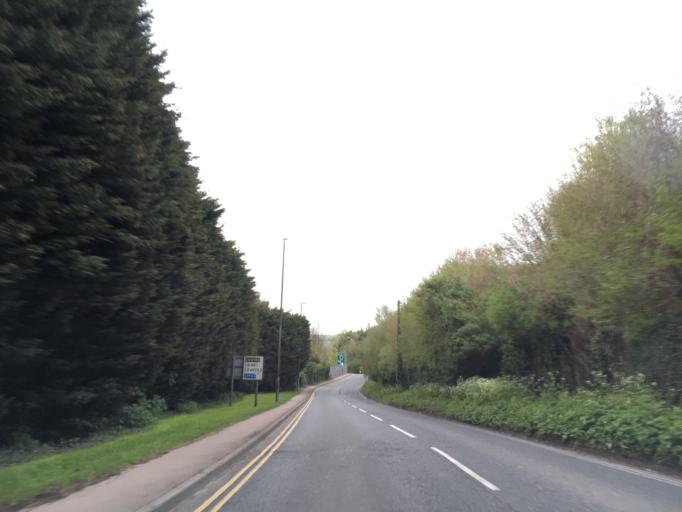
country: GB
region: England
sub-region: Gloucestershire
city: Stroud
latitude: 51.7363
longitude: -2.2340
